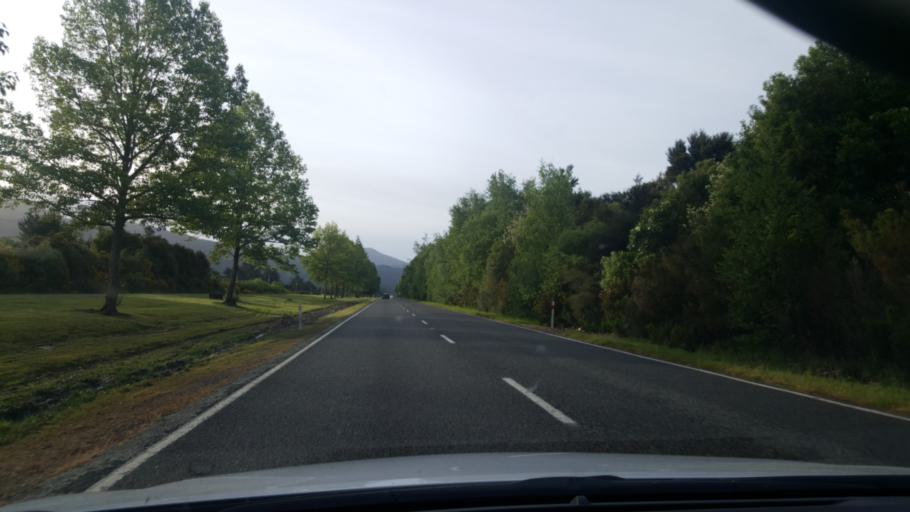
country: NZ
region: Waikato
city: Turangi
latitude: -38.9932
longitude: 175.7980
